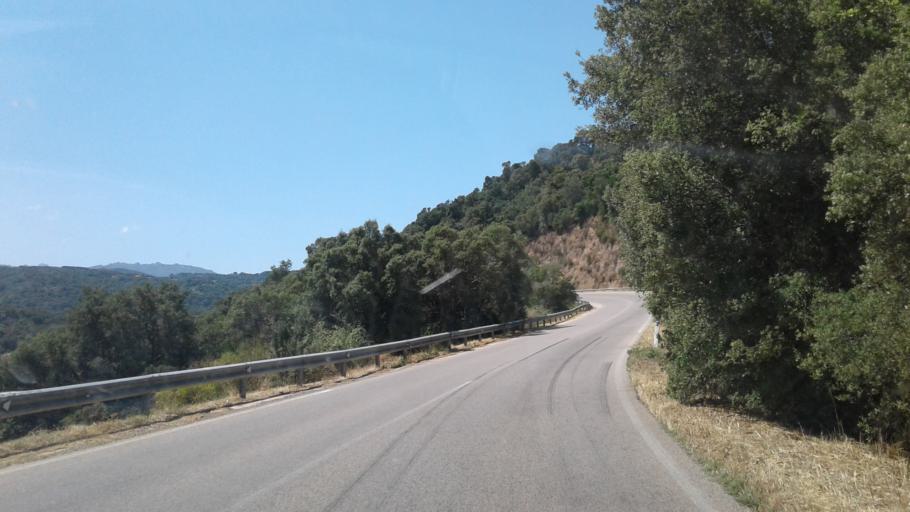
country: IT
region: Sardinia
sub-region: Provincia di Olbia-Tempio
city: Luras
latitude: 40.9499
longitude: 9.2013
